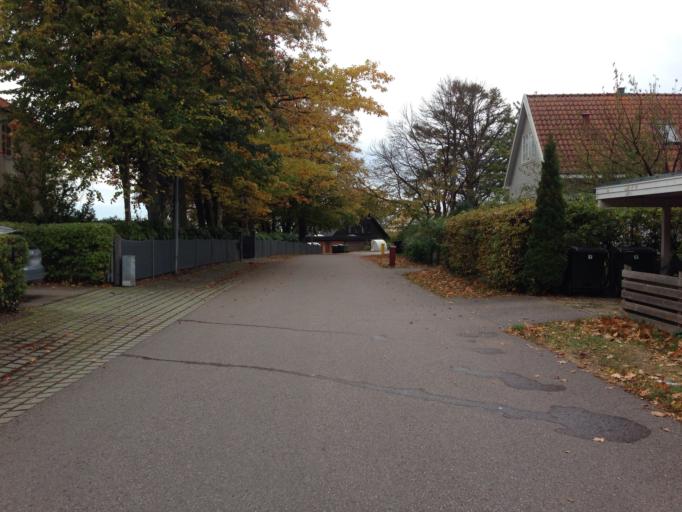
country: SE
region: Skane
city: Bjarred
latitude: 55.7135
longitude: 13.0251
